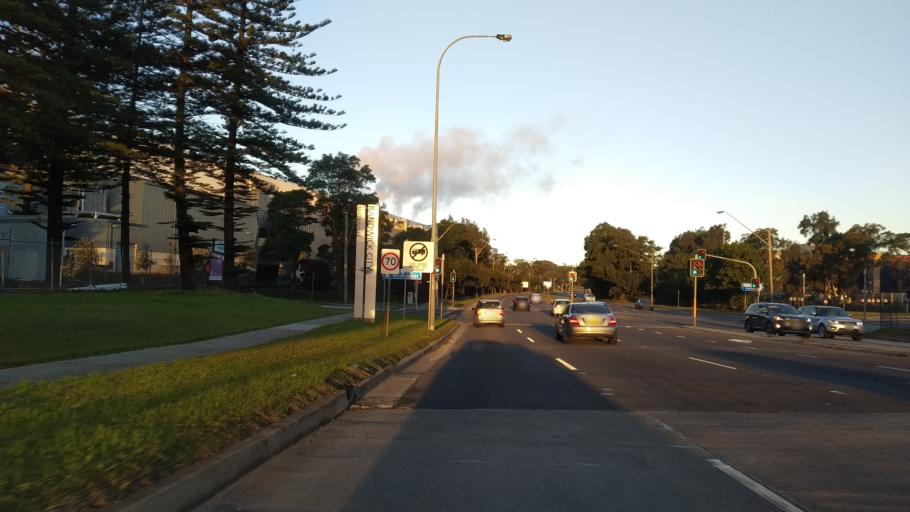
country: AU
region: New South Wales
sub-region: Randwick
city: Maroubra
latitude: -33.9635
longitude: 151.2210
